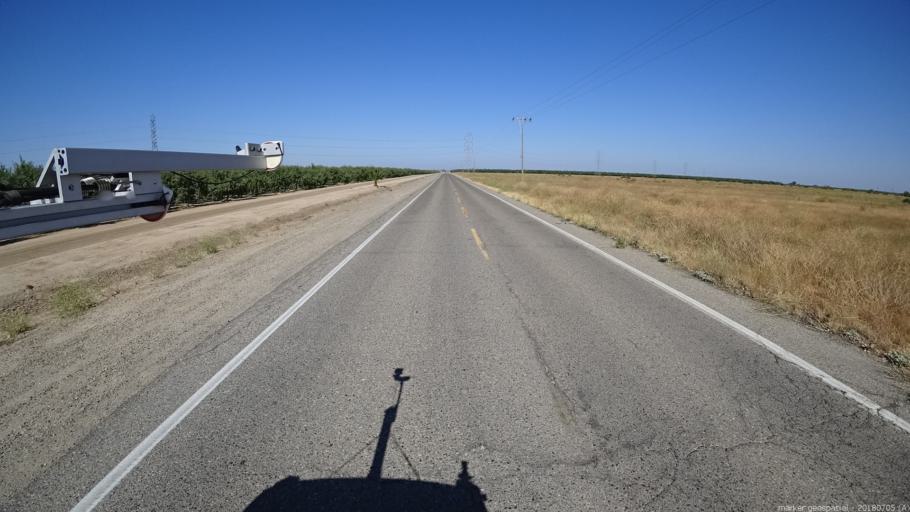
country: US
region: California
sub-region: Madera County
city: Fairmead
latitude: 37.1273
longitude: -120.2033
